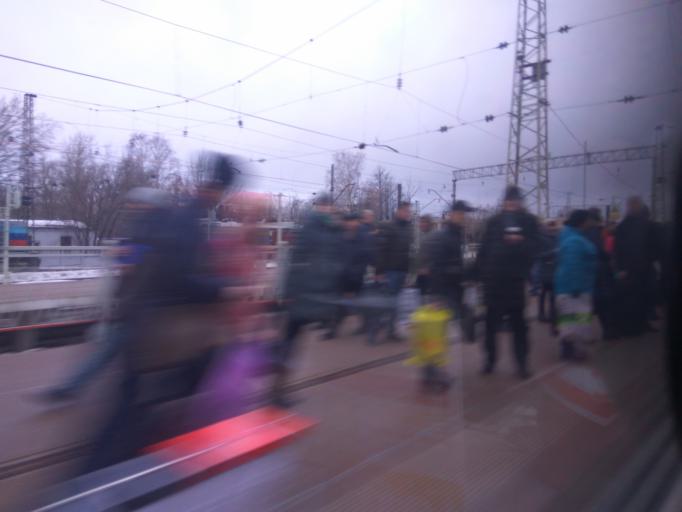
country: RU
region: Tverskaya
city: Tver
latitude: 56.8342
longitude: 35.8956
